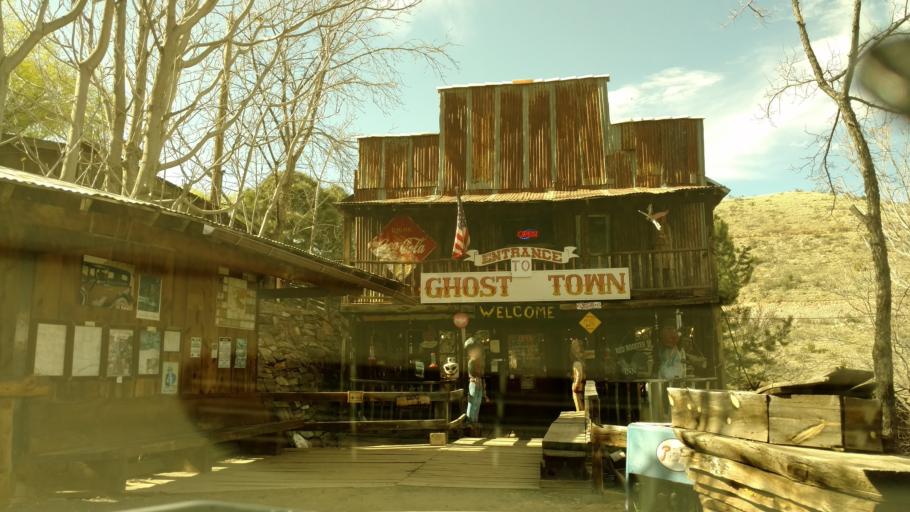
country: US
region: Arizona
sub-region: Yavapai County
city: Clarkdale
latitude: 34.7560
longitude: -112.1310
